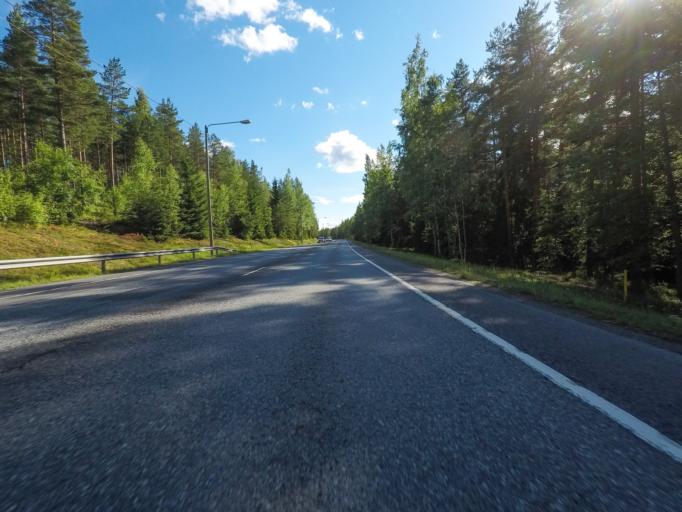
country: FI
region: Uusimaa
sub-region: Helsinki
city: Vihti
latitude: 60.3329
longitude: 24.2864
